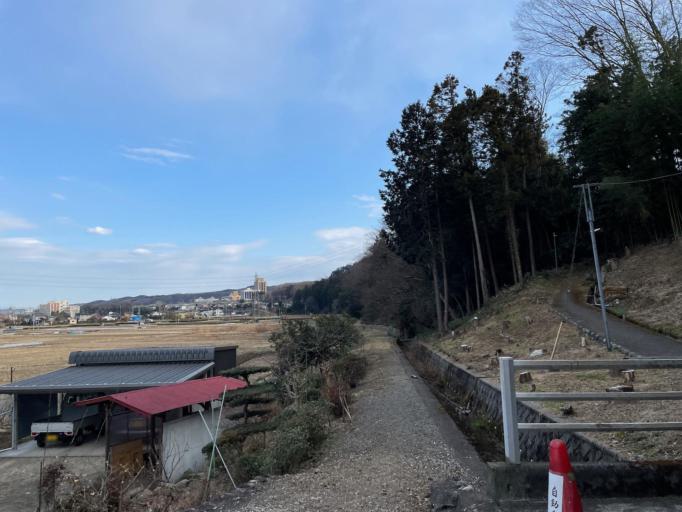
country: JP
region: Saitama
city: Hanno
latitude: 35.8357
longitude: 139.3211
